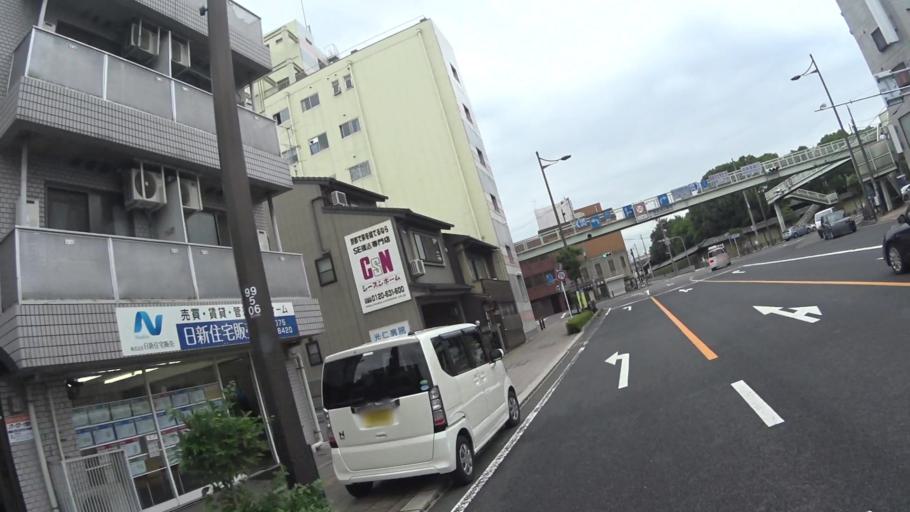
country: JP
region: Kyoto
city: Kyoto
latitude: 34.9786
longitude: 135.7458
